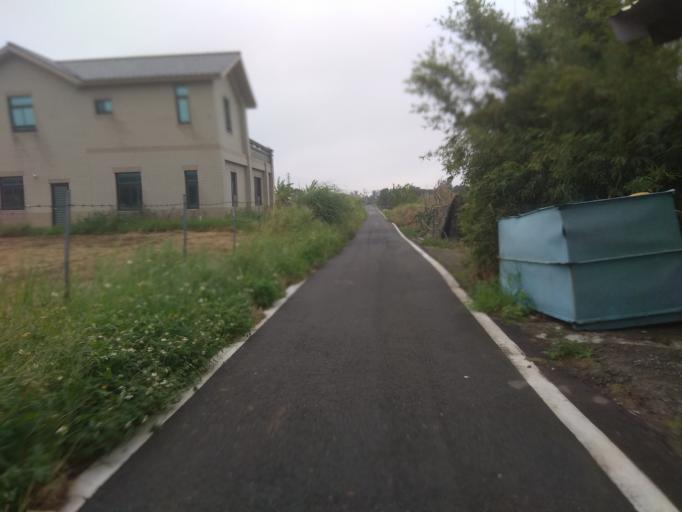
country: TW
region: Taiwan
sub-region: Hsinchu
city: Zhubei
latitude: 24.9922
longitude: 121.0344
